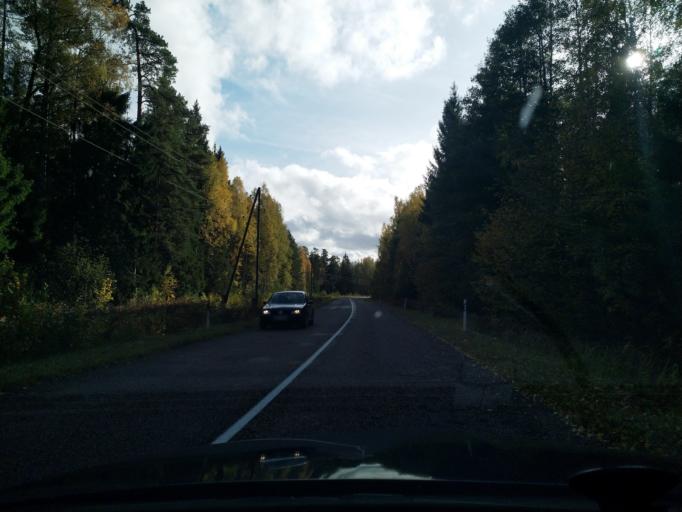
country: LV
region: Dundaga
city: Dundaga
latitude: 57.6460
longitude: 22.2645
